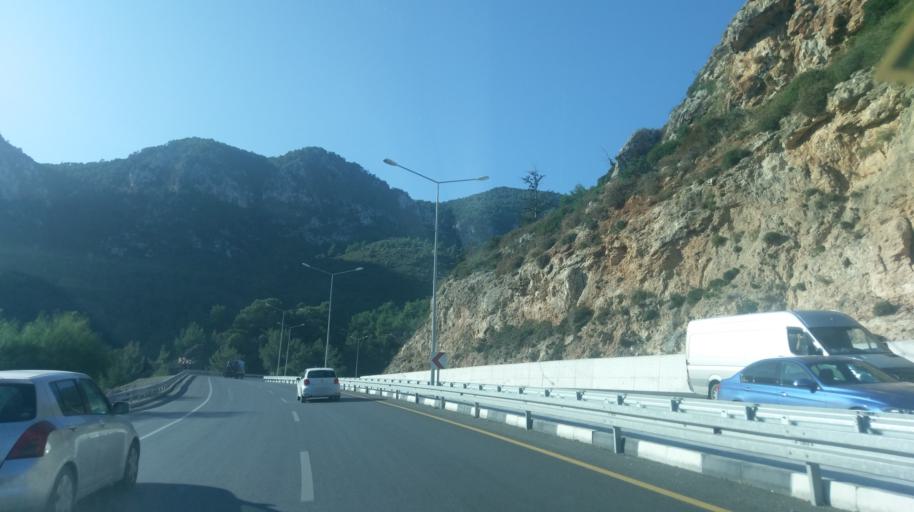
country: CY
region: Keryneia
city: Kyrenia
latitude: 35.3086
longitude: 33.3225
